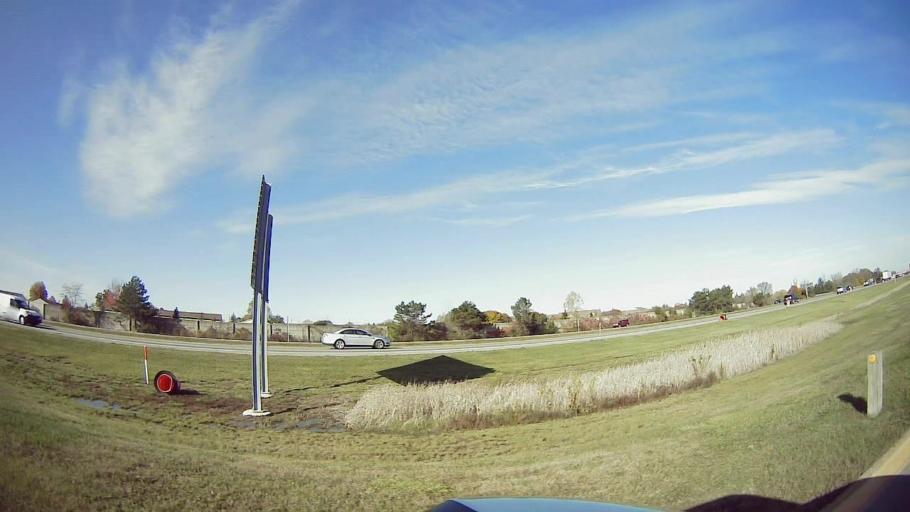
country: US
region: Michigan
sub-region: Wayne County
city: Canton
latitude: 42.3009
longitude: -83.4423
